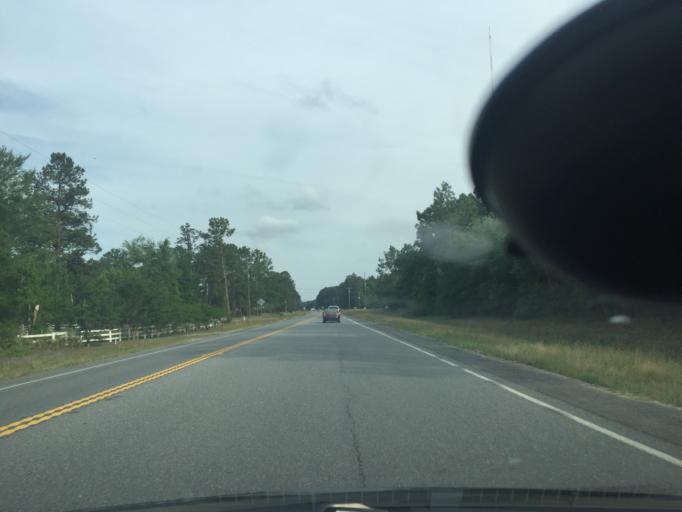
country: US
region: Georgia
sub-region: Chatham County
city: Bloomingdale
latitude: 32.0545
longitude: -81.3448
